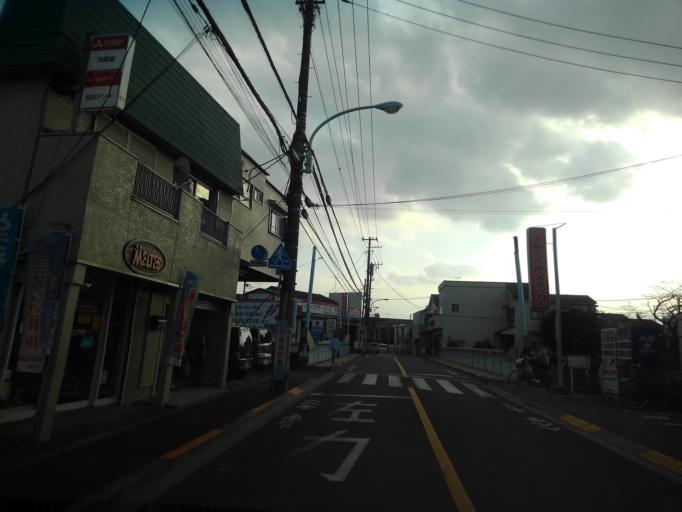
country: JP
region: Tokyo
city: Chofugaoka
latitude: 35.6597
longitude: 139.5521
